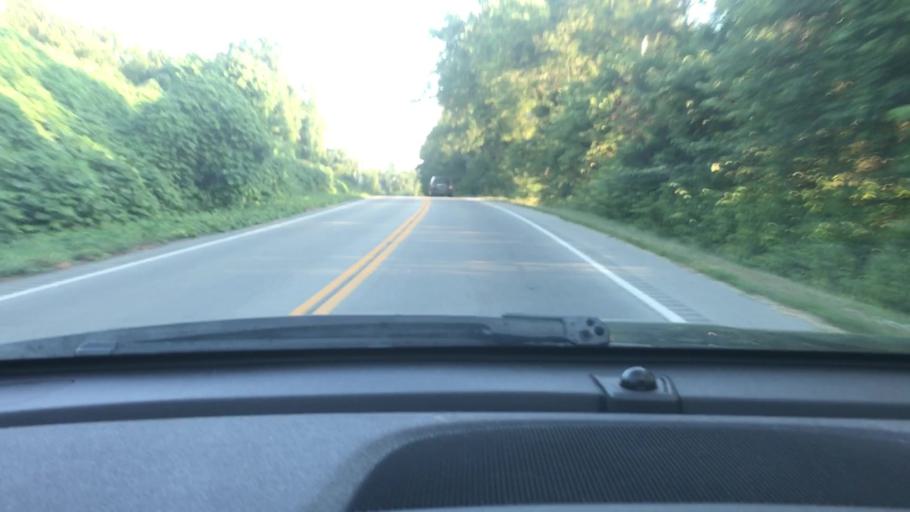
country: US
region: Tennessee
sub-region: Dickson County
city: Charlotte
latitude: 36.1555
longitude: -87.3562
